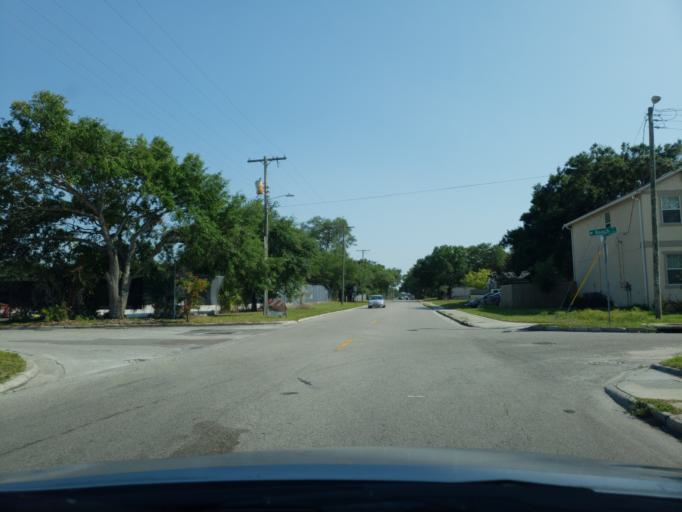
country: US
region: Florida
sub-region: Hillsborough County
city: Tampa
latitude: 27.9632
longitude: -82.4766
